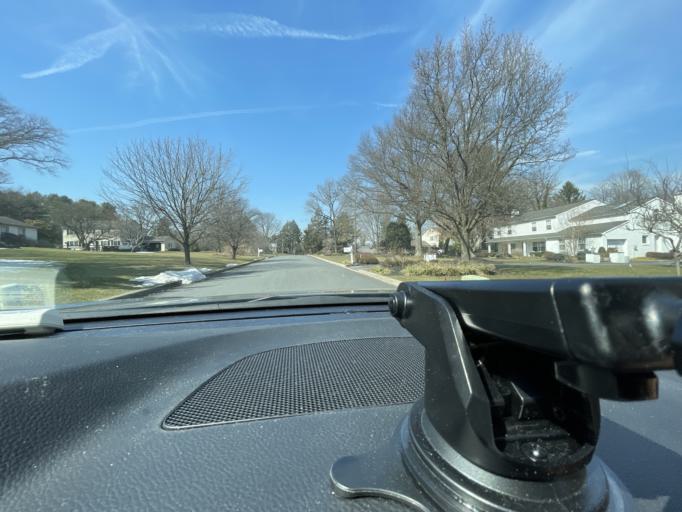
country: US
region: Pennsylvania
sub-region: Montgomery County
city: Blue Bell
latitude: 40.1589
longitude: -75.2589
